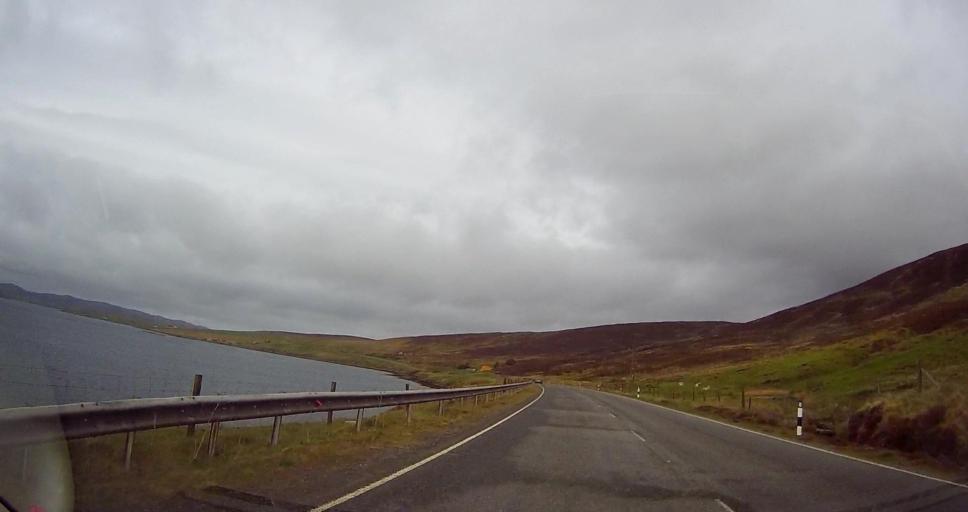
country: GB
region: Scotland
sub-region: Shetland Islands
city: Lerwick
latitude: 60.3659
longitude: -1.2900
